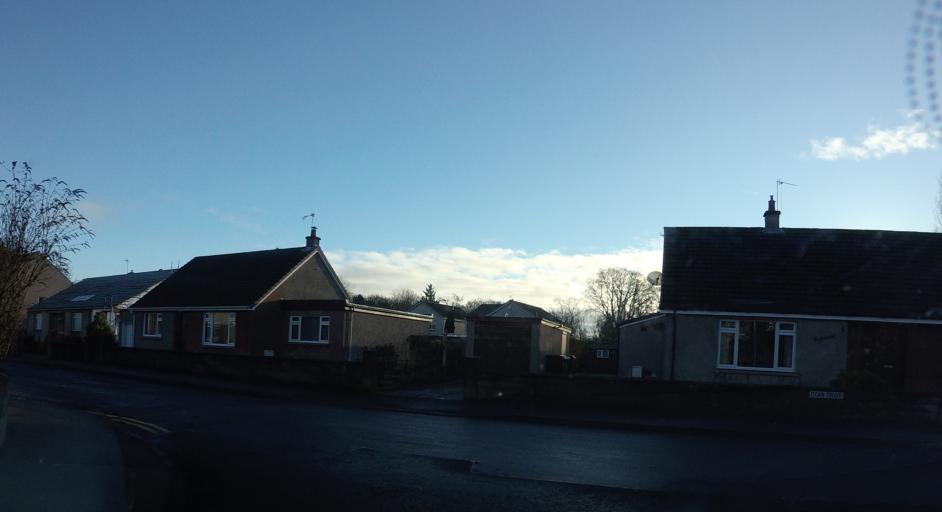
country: GB
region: Scotland
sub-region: Fife
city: Crossford
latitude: 56.0639
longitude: -3.5027
